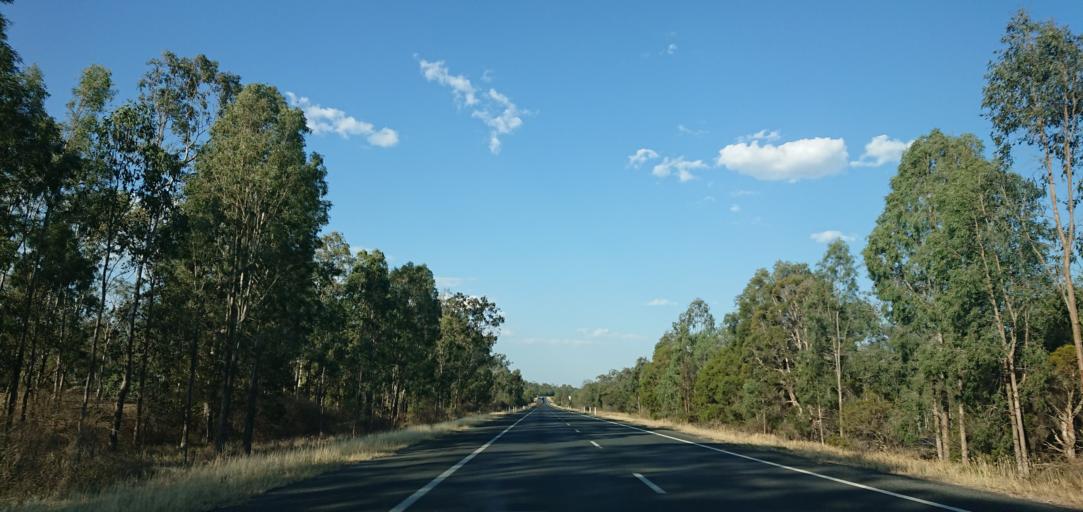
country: AU
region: Queensland
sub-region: Lockyer Valley
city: Gatton
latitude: -27.5390
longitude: 152.2445
